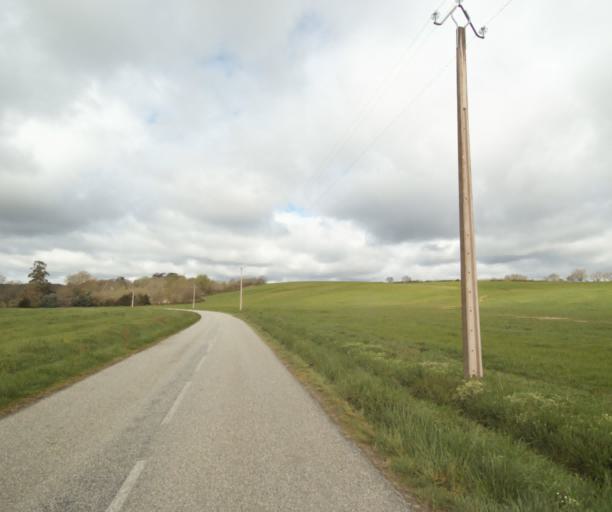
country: FR
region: Midi-Pyrenees
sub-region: Departement de l'Ariege
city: Saverdun
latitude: 43.2270
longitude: 1.5563
